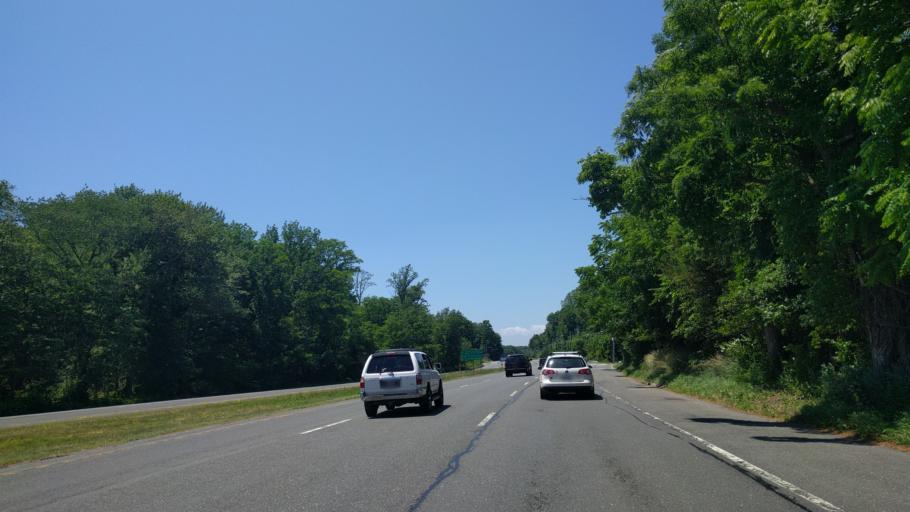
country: US
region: New York
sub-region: Suffolk County
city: Hauppauge
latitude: 40.8248
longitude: -73.2147
